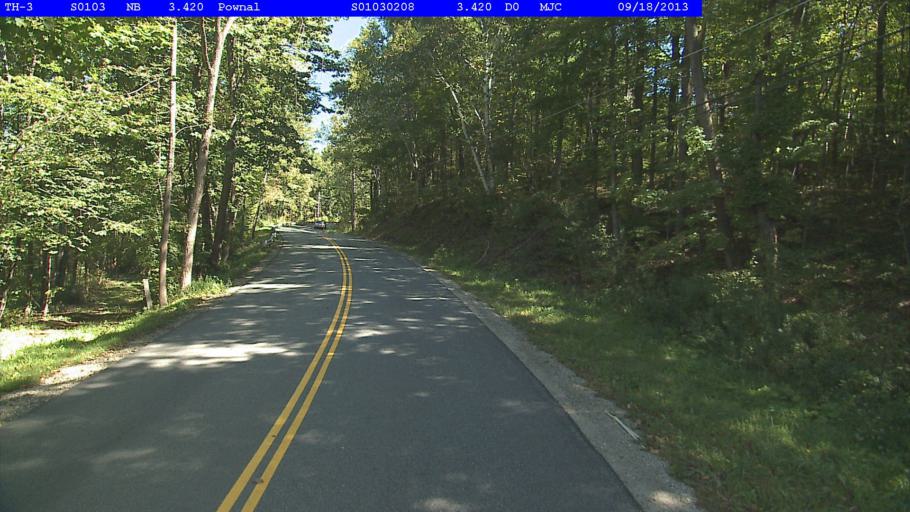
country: US
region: Vermont
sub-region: Bennington County
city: Bennington
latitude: 42.7958
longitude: -73.2126
